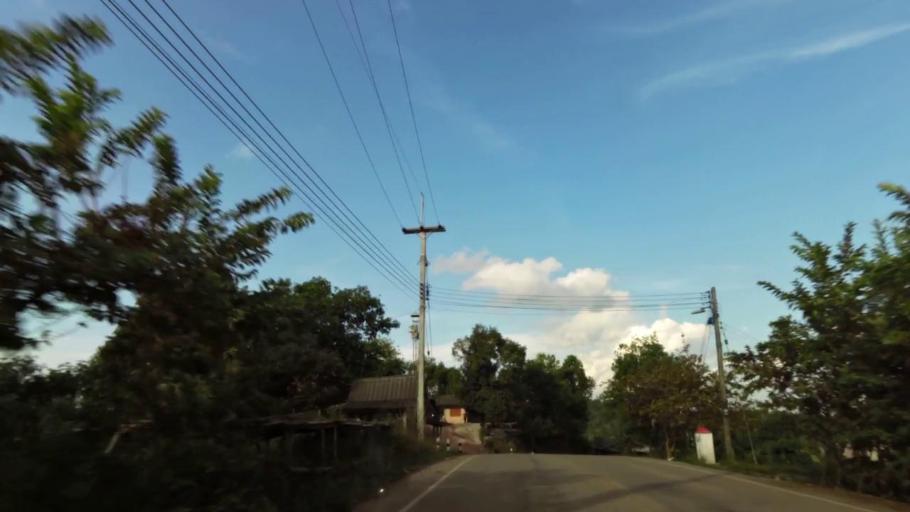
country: TH
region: Chiang Rai
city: Khun Tan
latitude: 19.8704
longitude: 100.3400
